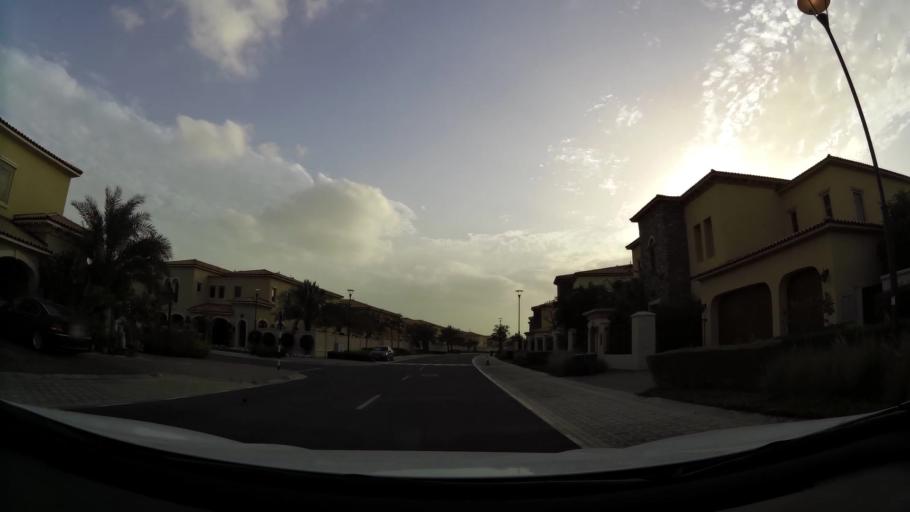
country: AE
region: Abu Dhabi
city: Abu Dhabi
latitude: 24.5366
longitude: 54.4345
